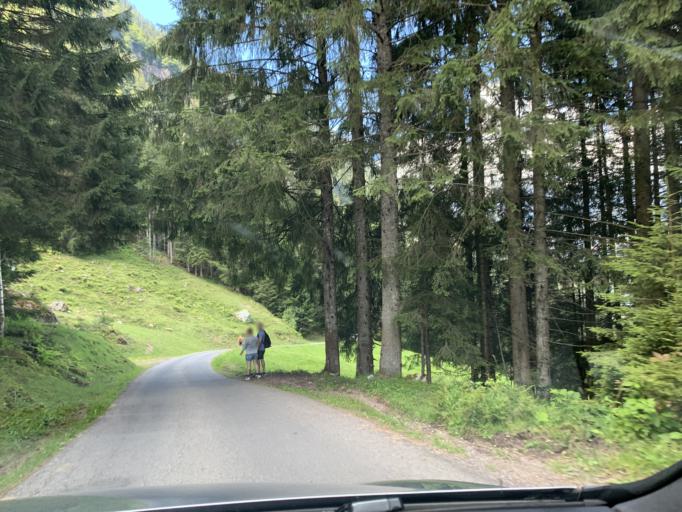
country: CH
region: Saint Gallen
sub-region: Wahlkreis Sarganserland
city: Quarten
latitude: 47.0805
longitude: 9.1981
